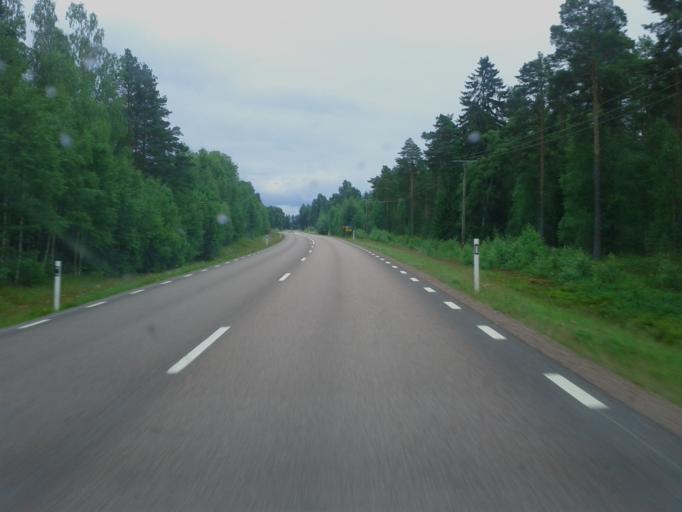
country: SE
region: Dalarna
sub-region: Mora Kommun
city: Mora
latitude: 61.0334
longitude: 14.5149
